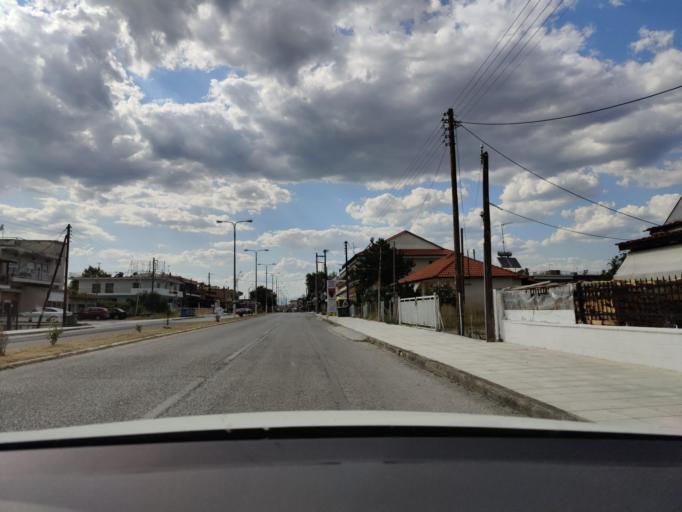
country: GR
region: Central Macedonia
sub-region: Nomos Serron
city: Lefkonas
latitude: 41.0970
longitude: 23.4999
